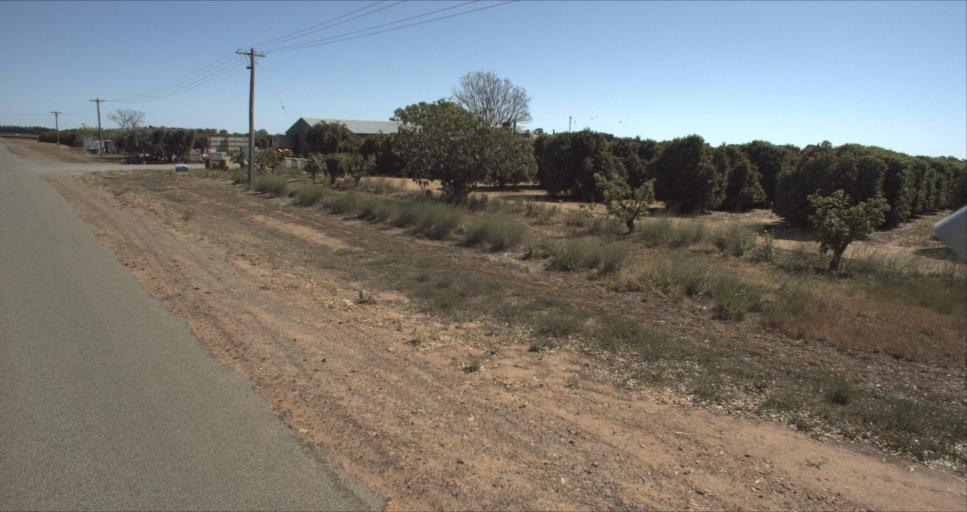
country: AU
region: New South Wales
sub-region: Leeton
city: Leeton
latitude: -34.5378
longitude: 146.3344
